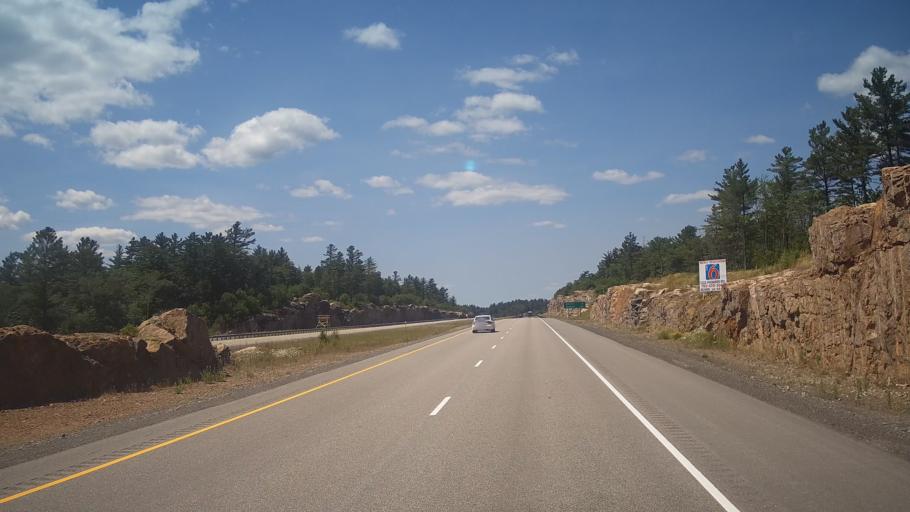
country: CA
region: Ontario
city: Greater Sudbury
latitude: 46.1988
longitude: -80.7523
